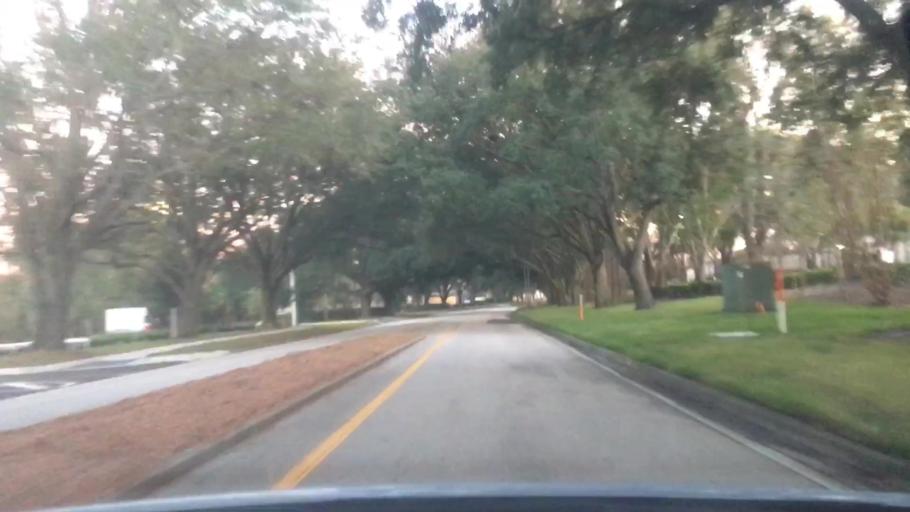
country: US
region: Florida
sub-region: Duval County
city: Jacksonville
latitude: 30.2589
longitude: -81.5941
